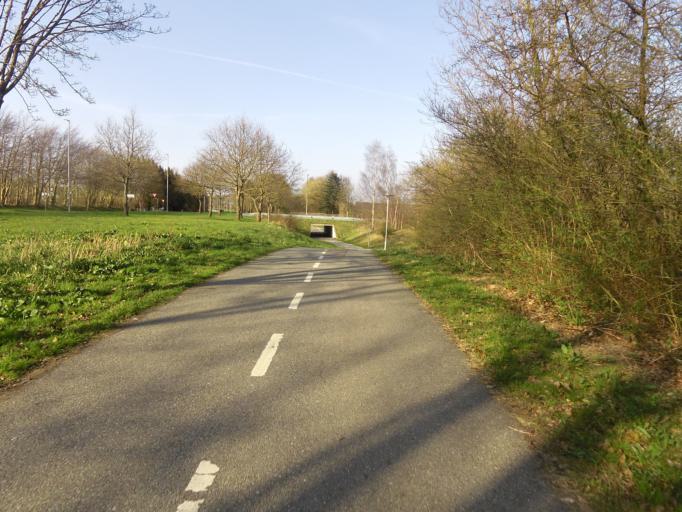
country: DK
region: South Denmark
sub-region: Vejen Kommune
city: Vejen
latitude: 55.4658
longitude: 9.1195
